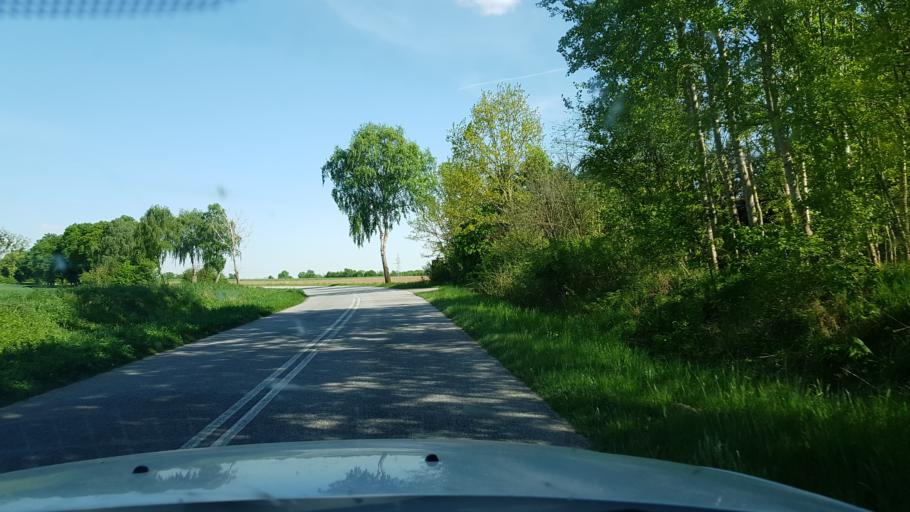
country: PL
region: West Pomeranian Voivodeship
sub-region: Powiat lobeski
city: Resko
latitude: 53.8116
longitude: 15.4089
